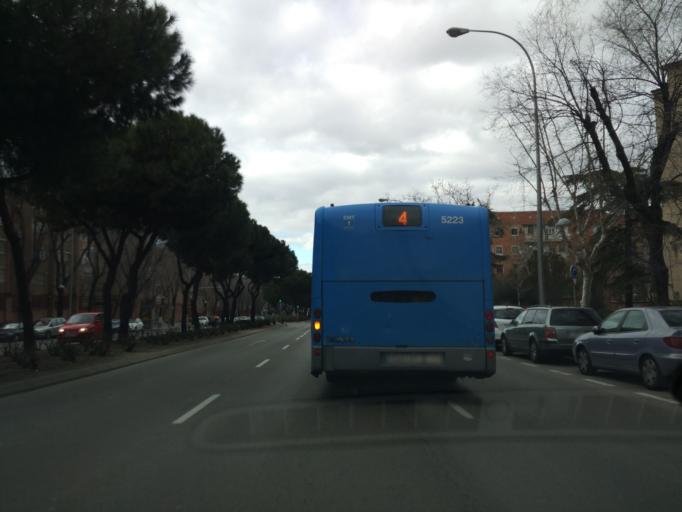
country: ES
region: Madrid
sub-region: Provincia de Madrid
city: San Blas
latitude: 40.4272
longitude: -3.6301
